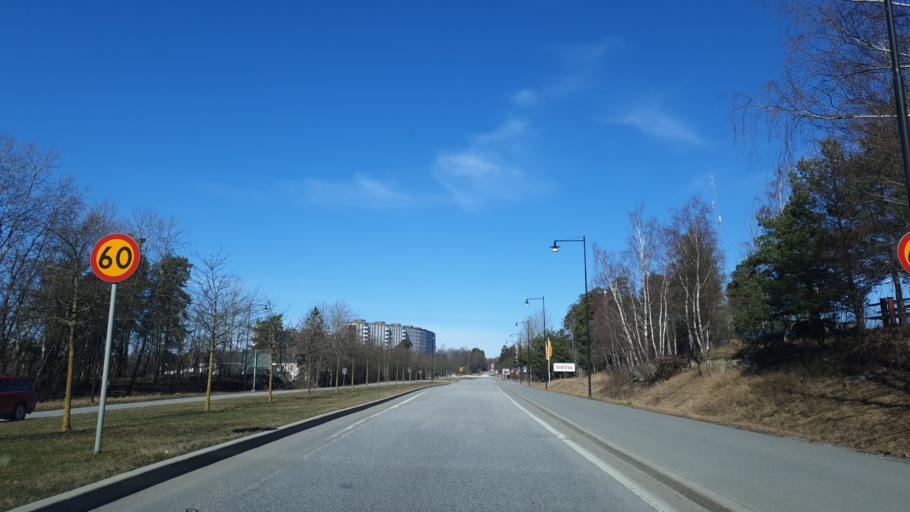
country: SE
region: Stockholm
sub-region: Jarfalla Kommun
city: Jakobsberg
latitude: 59.4224
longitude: 17.8490
